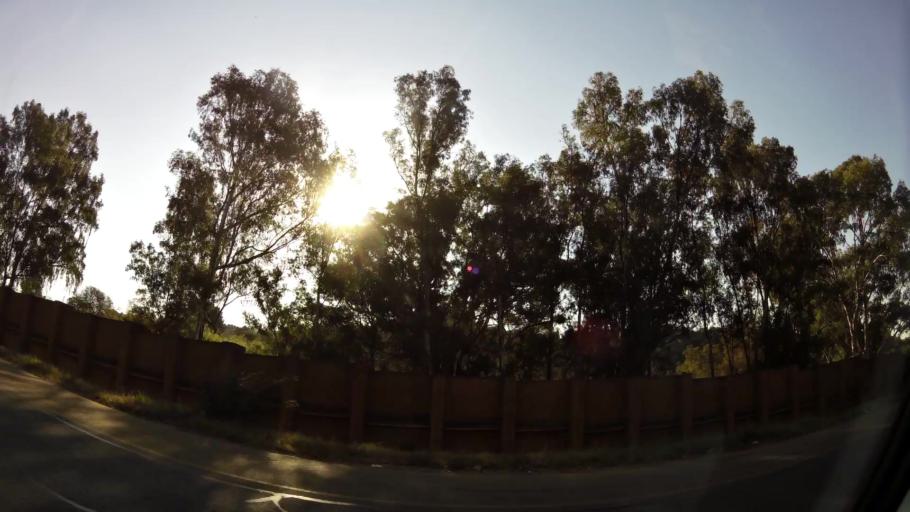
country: ZA
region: Gauteng
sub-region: City of Tshwane Metropolitan Municipality
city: Pretoria
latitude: -25.7825
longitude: 28.3339
